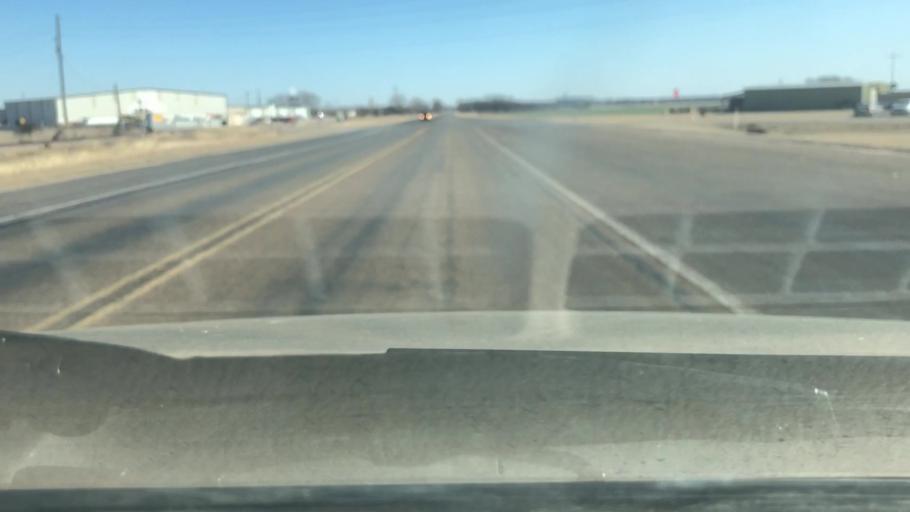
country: US
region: Kansas
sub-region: Harvey County
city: North Newton
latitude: 38.0871
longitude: -97.3715
